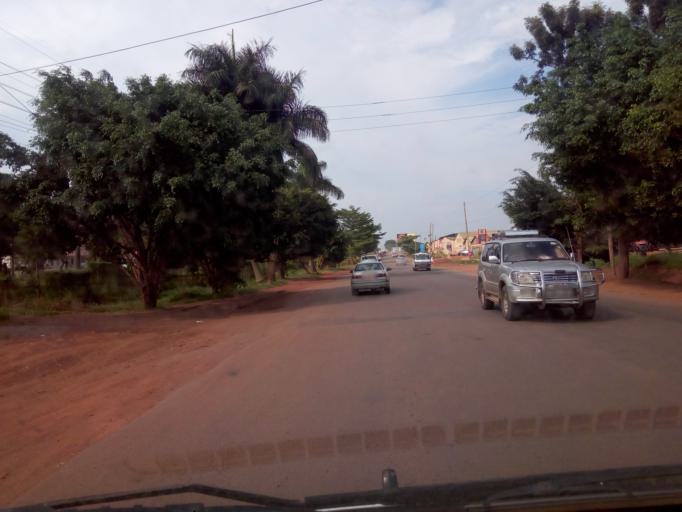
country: UG
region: Central Region
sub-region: Wakiso District
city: Kireka
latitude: 0.3385
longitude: 32.6259
